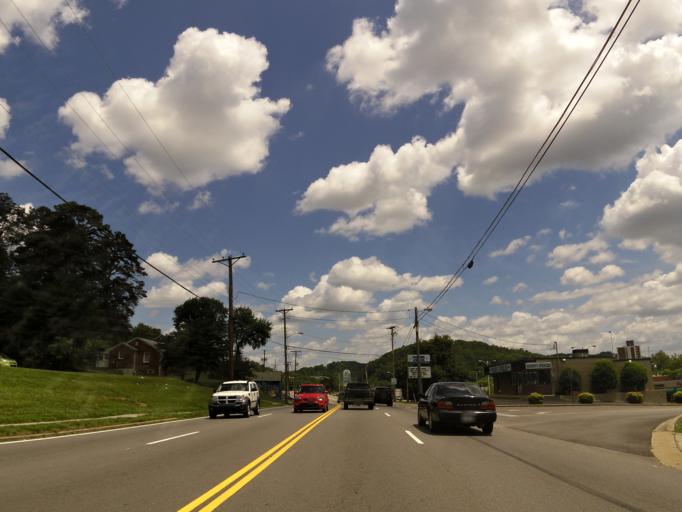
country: US
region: Tennessee
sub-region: Knox County
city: Knoxville
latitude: 36.0109
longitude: -83.9246
